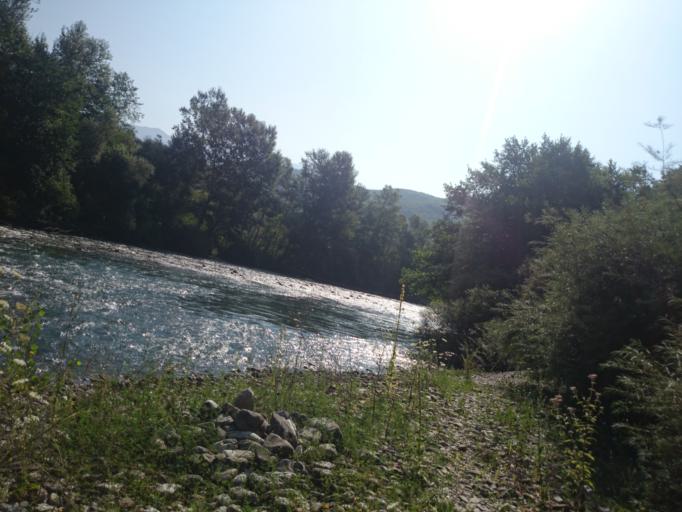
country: AL
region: Diber
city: Peshkopi
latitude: 41.6407
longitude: 20.4067
